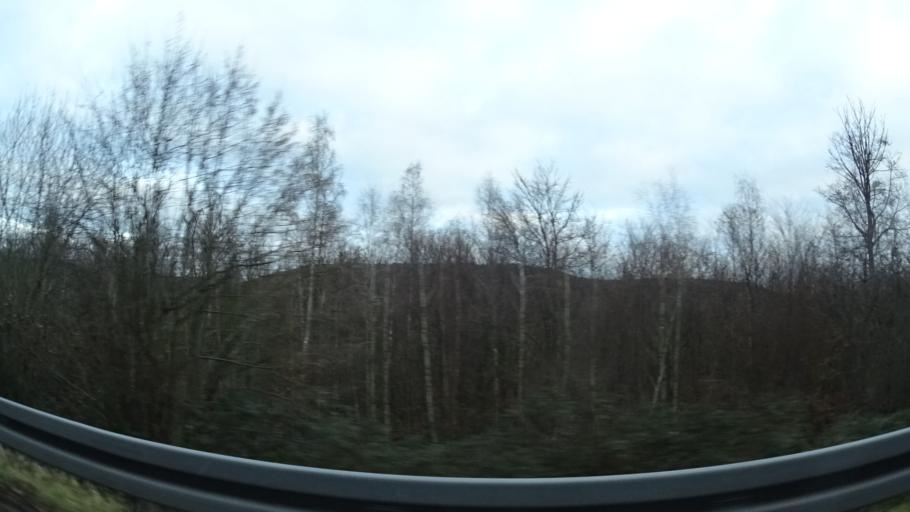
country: DE
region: Bavaria
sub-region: Regierungsbezirk Unterfranken
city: Miltenberg
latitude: 49.7009
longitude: 9.2940
